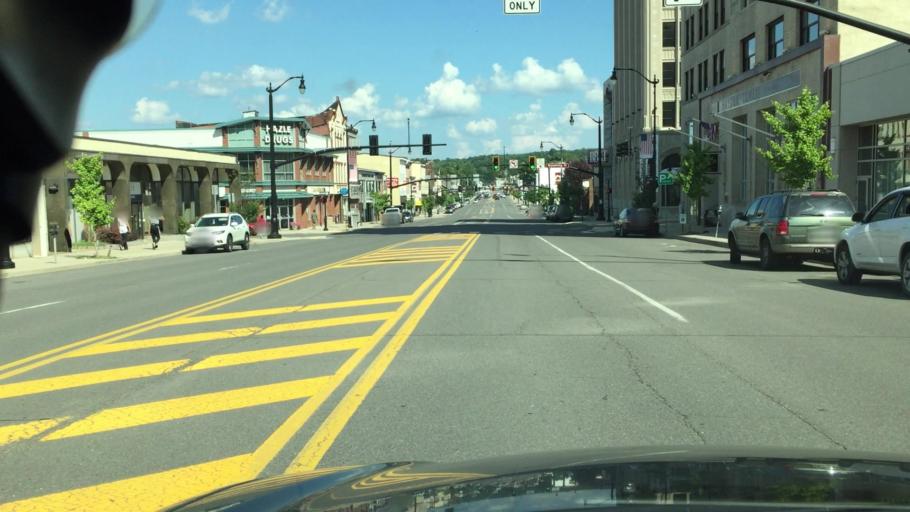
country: US
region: Pennsylvania
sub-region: Luzerne County
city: Hazleton
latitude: 40.9542
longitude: -75.9748
